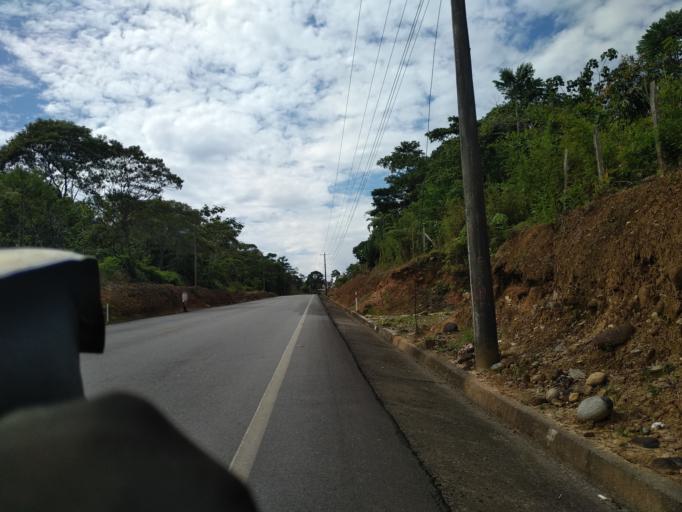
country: EC
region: Napo
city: Tena
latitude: -1.1200
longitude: -77.8104
